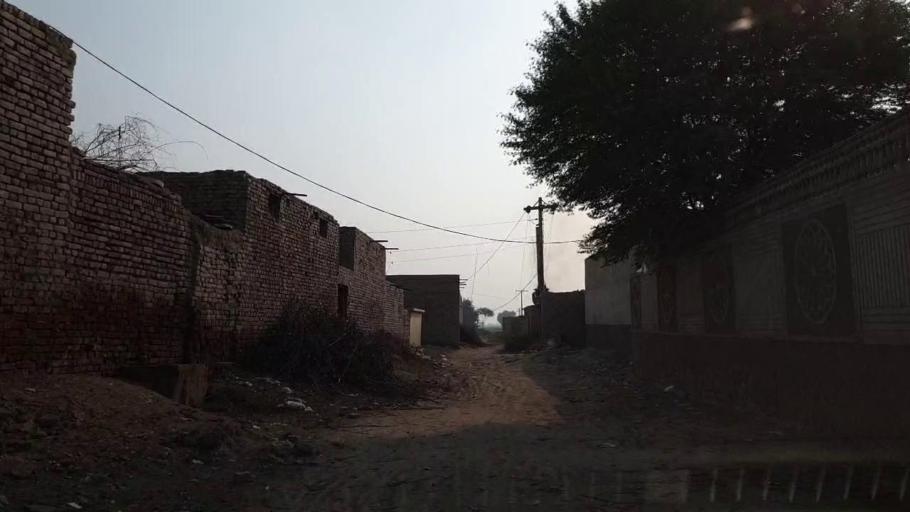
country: PK
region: Sindh
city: Bhan
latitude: 26.5598
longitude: 67.7035
